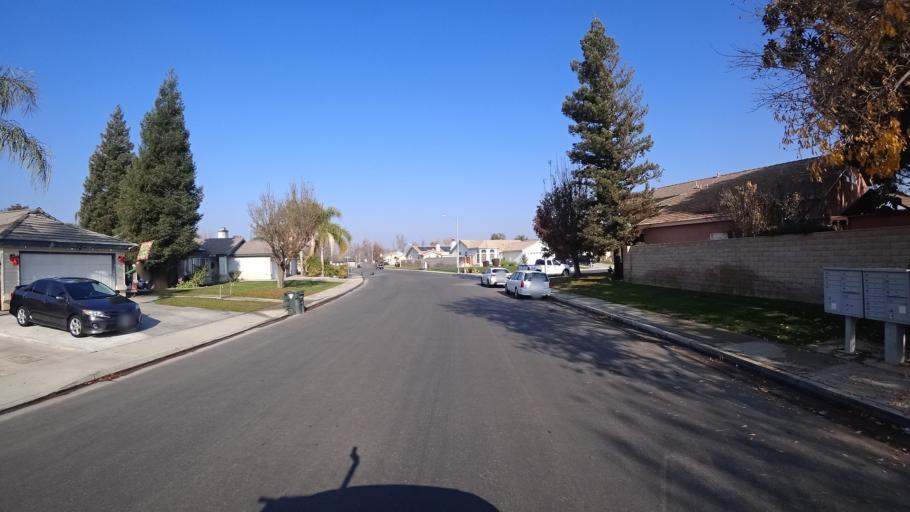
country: US
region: California
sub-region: Kern County
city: Greenacres
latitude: 35.3899
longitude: -119.1041
